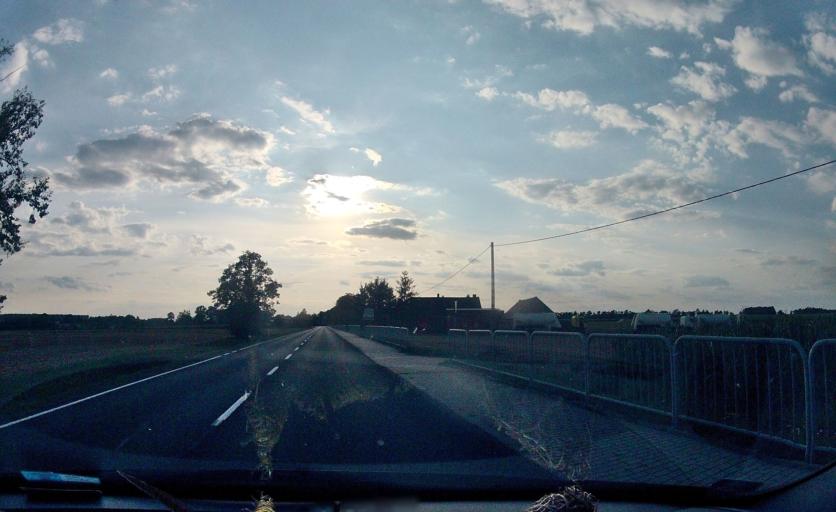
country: PL
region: Opole Voivodeship
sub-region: Powiat oleski
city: Gorzow Slaski
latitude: 51.0022
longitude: 18.3248
